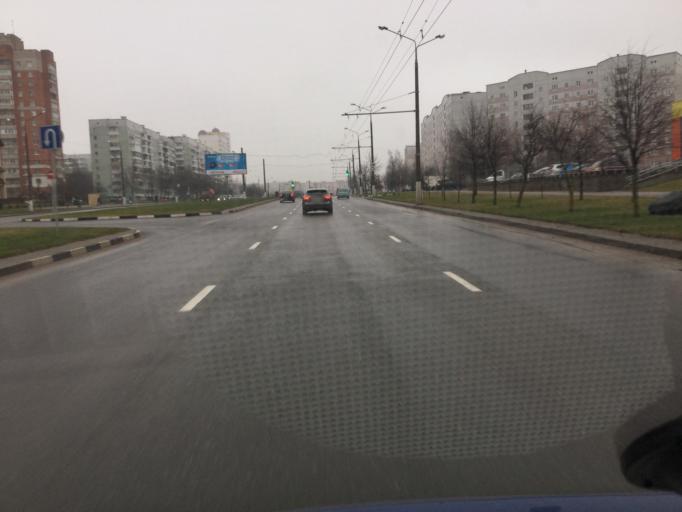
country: BY
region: Vitebsk
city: Vitebsk
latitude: 55.1630
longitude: 30.2134
